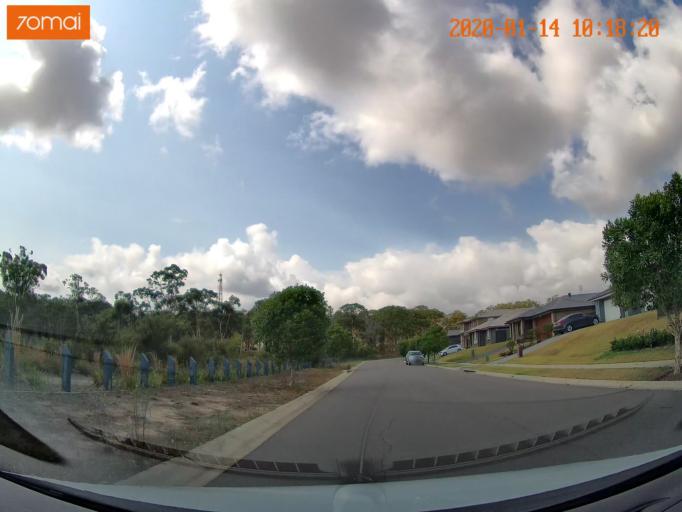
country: AU
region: New South Wales
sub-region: Lake Macquarie Shire
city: Dora Creek
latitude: -33.1101
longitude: 151.5113
